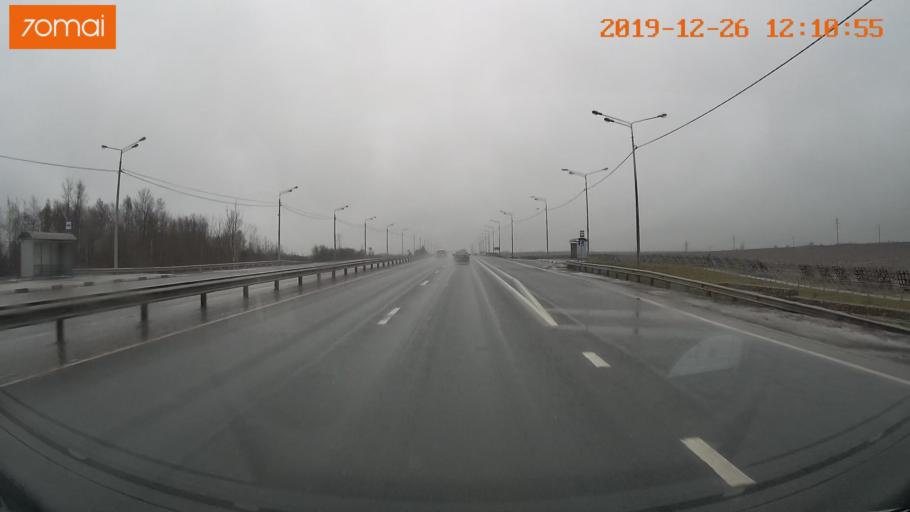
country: RU
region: Vologda
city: Tonshalovo
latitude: 59.2543
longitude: 37.9757
